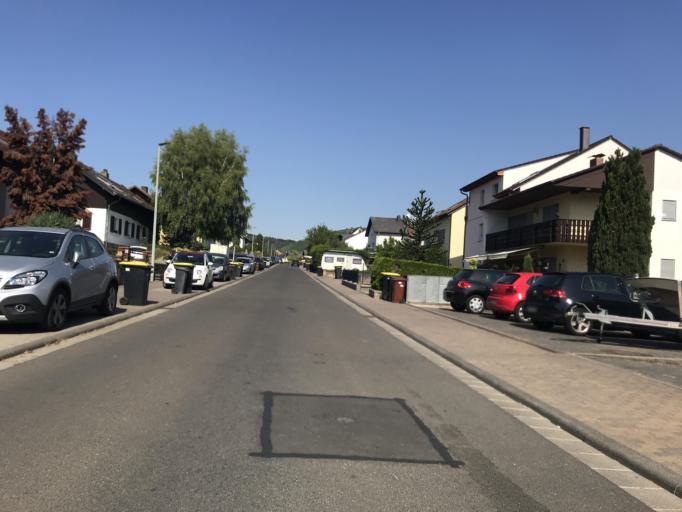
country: DE
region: Hesse
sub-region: Regierungsbezirk Darmstadt
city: Eltville
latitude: 50.0389
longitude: 8.1129
